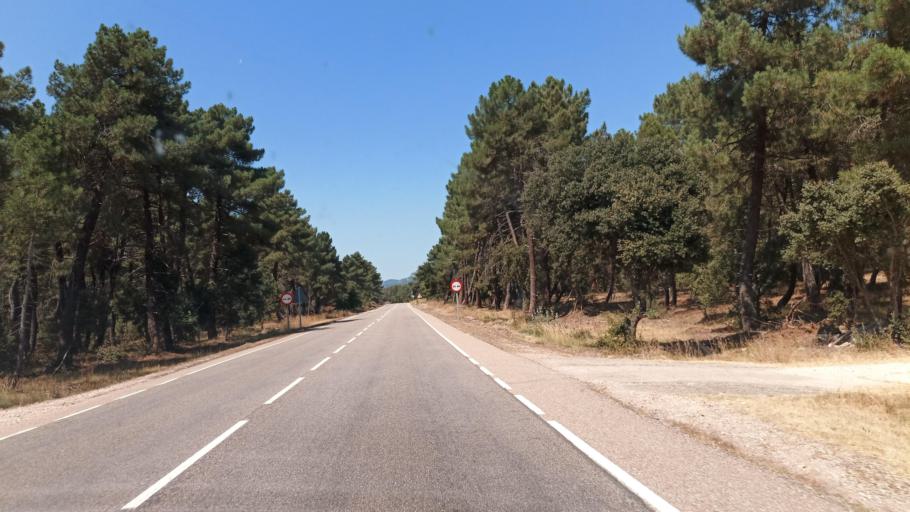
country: ES
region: Castille and Leon
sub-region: Provincia de Burgos
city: Ona
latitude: 42.6693
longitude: -3.4109
